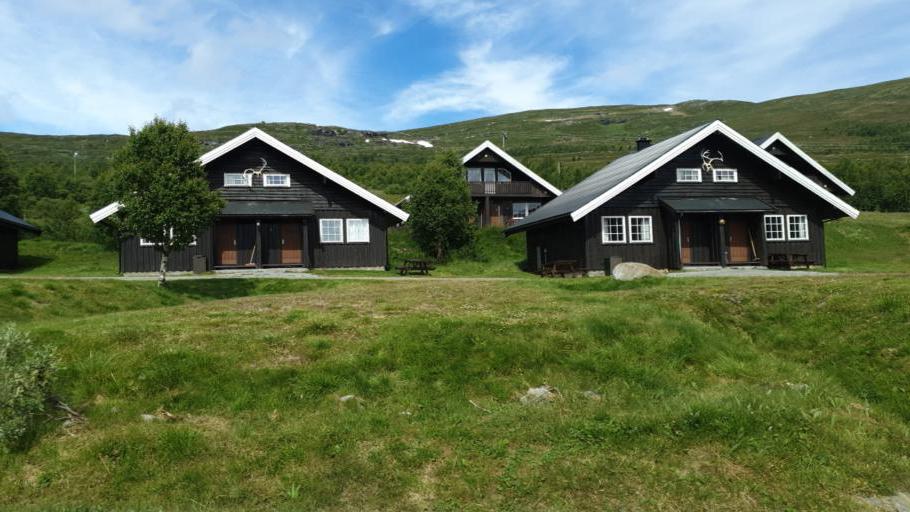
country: NO
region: Oppland
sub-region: Oystre Slidre
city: Heggenes
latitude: 61.5140
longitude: 8.8520
